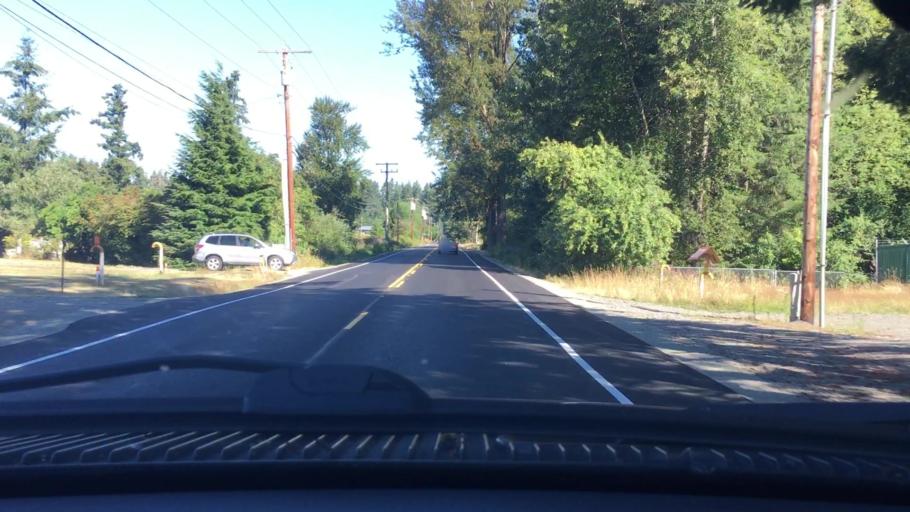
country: US
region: Washington
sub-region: King County
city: Lake Morton-Berrydale
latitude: 47.3227
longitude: -122.1089
